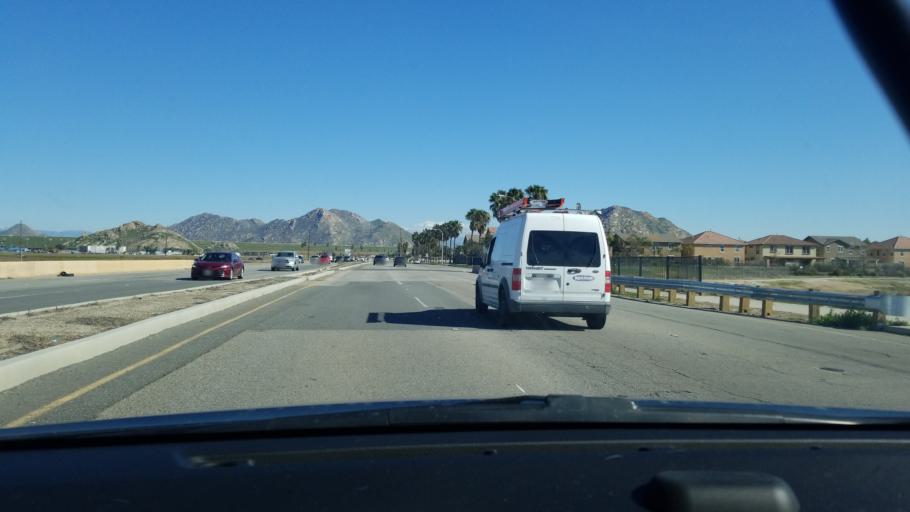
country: US
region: California
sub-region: Riverside County
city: Perris
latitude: 33.8445
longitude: -117.2136
